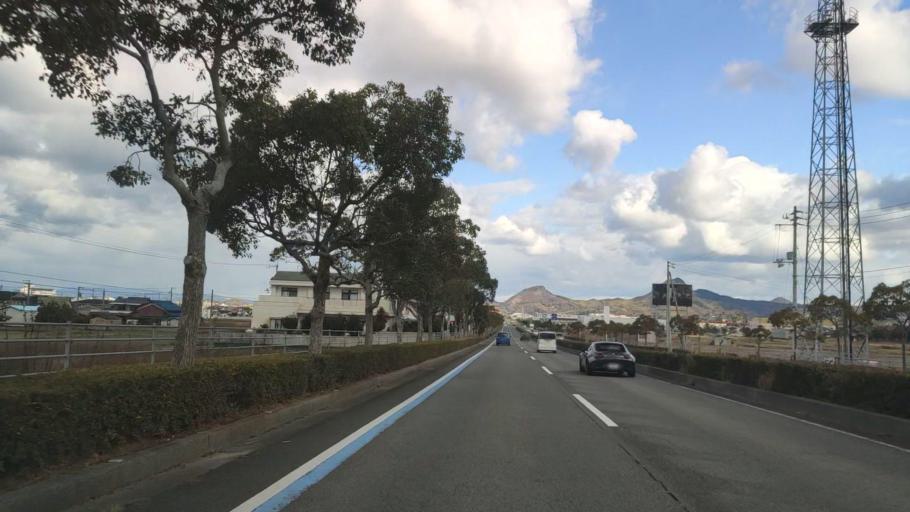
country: JP
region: Ehime
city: Hojo
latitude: 33.9554
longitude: 132.7758
